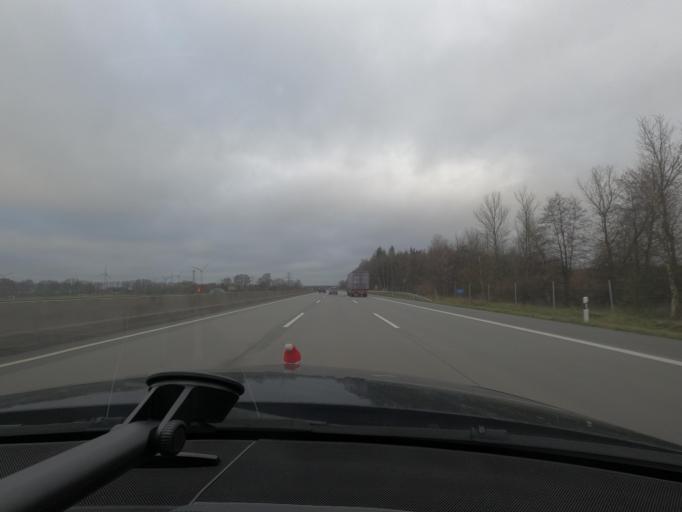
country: DE
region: Schleswig-Holstein
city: Bimohlen
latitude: 53.9498
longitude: 9.9498
